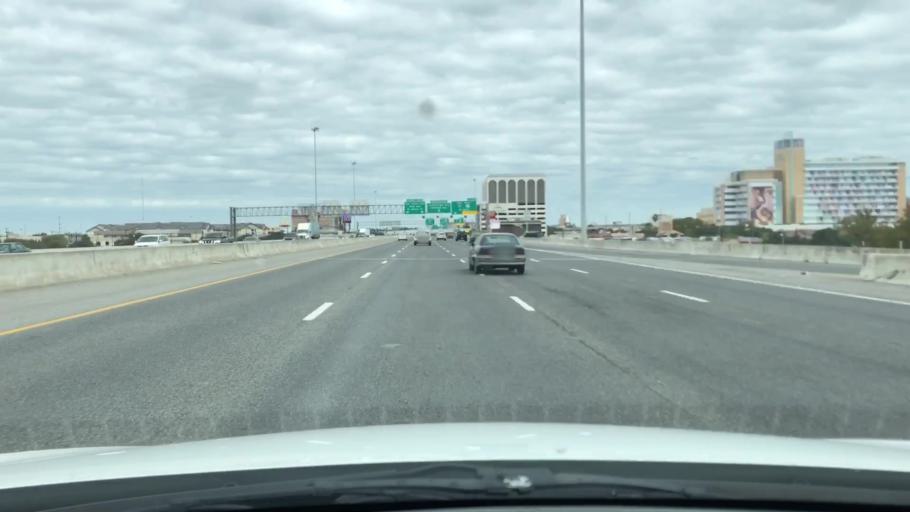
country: US
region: Texas
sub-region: Bexar County
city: San Antonio
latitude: 29.4229
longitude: -98.5014
